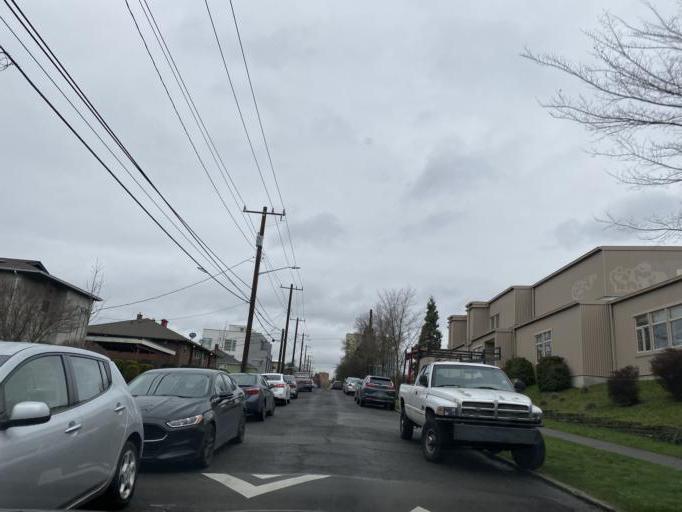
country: US
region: Washington
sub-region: King County
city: Seattle
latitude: 47.5849
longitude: -122.3160
